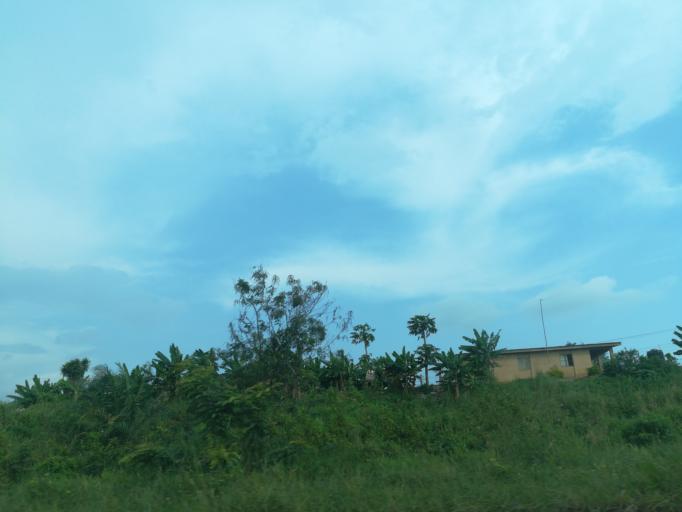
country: NG
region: Lagos
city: Ikorodu
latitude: 6.6240
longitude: 3.6629
